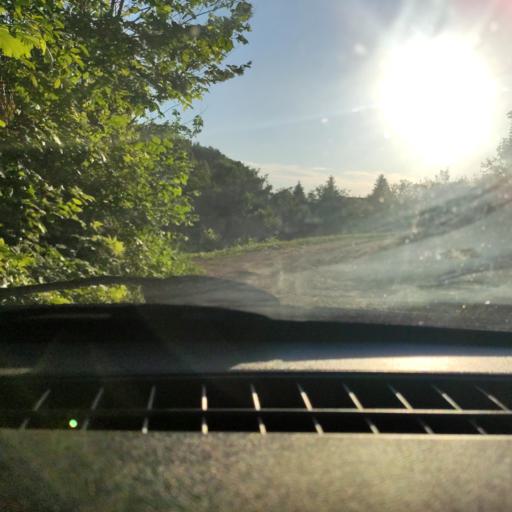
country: RU
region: Bashkortostan
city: Avdon
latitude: 54.6140
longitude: 55.6844
